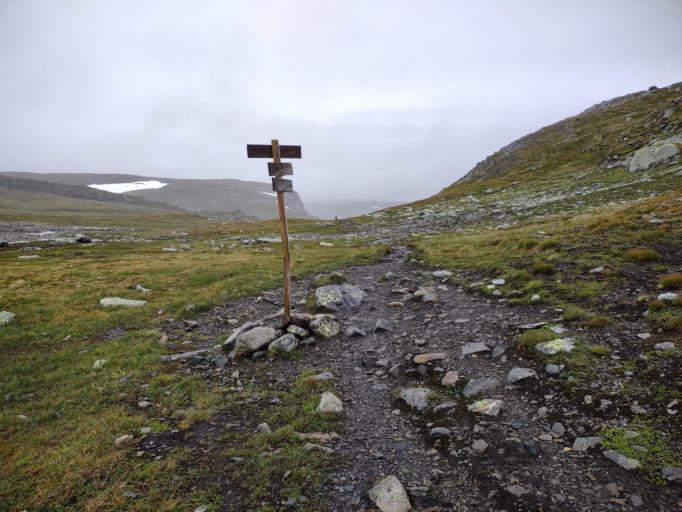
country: NO
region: Hordaland
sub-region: Eidfjord
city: Eidfjord
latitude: 60.0672
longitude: 7.1338
